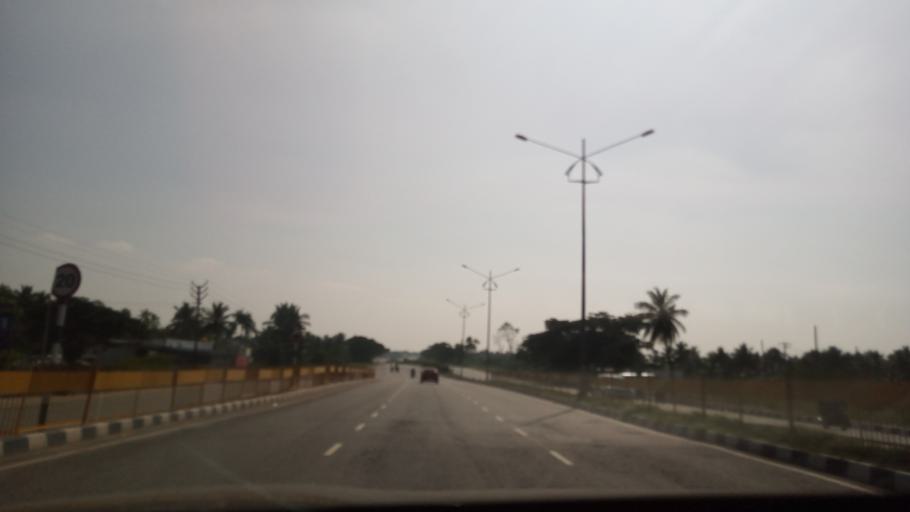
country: IN
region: Tamil Nadu
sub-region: Vellore
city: Jolarpettai
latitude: 12.6316
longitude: 78.5688
